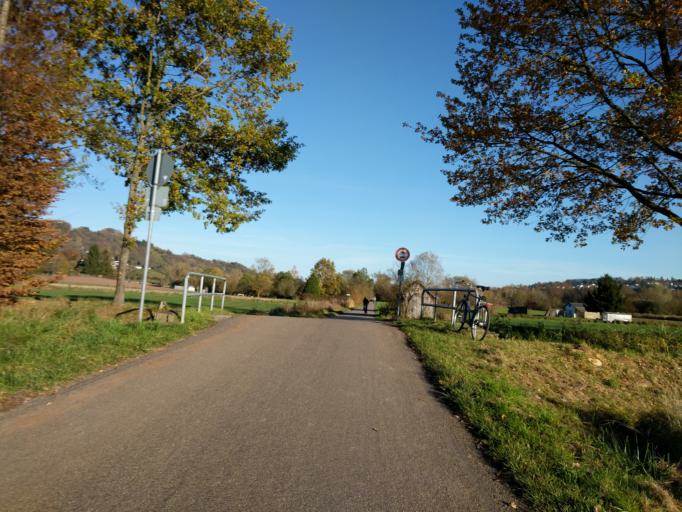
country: DE
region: Baden-Wuerttemberg
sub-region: Tuebingen Region
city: Tuebingen
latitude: 48.5224
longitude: 9.0134
